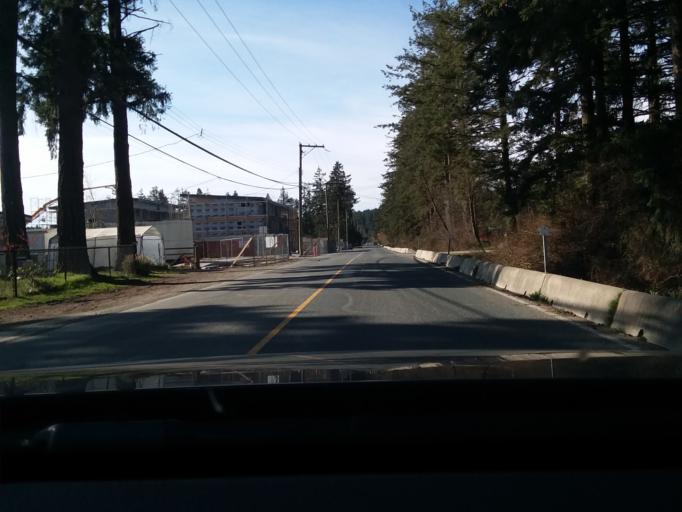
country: CA
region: British Columbia
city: Langford
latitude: 48.4287
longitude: -123.5355
